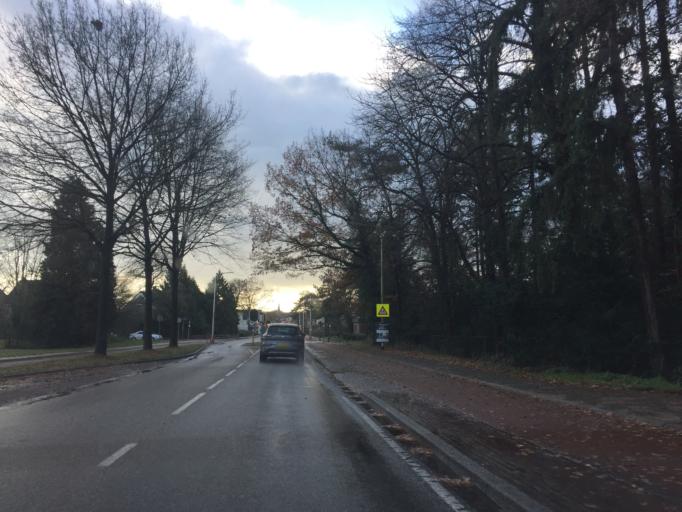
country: NL
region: Utrecht
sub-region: Gemeente Utrechtse Heuvelrug
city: Doorn
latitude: 52.0404
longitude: 5.3462
